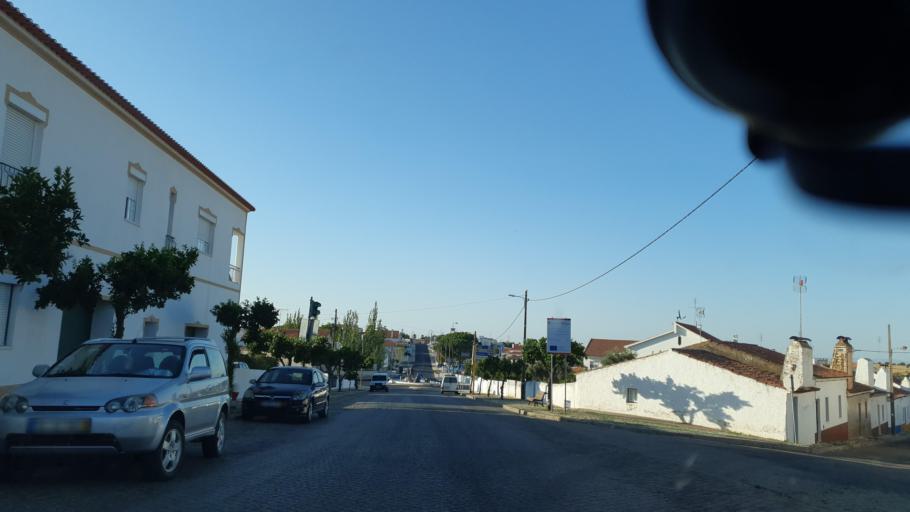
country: PT
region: Portalegre
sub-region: Fronteira
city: Fronteira
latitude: 38.9560
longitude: -7.6747
